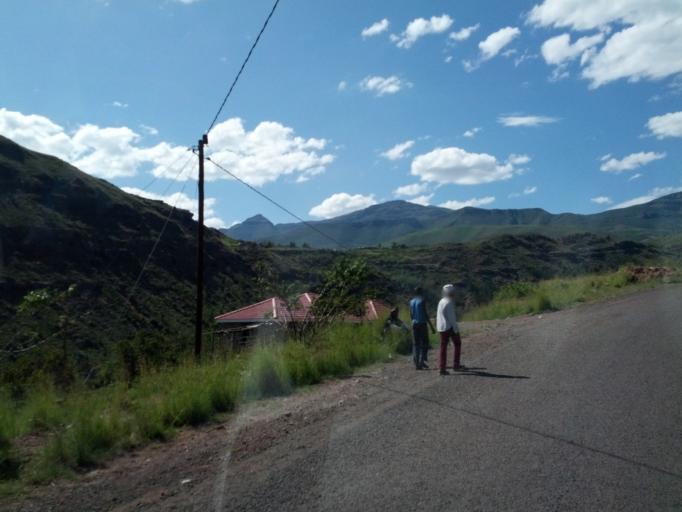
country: LS
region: Qacha's Nek
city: Qacha's Nek
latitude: -30.0599
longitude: 28.4748
